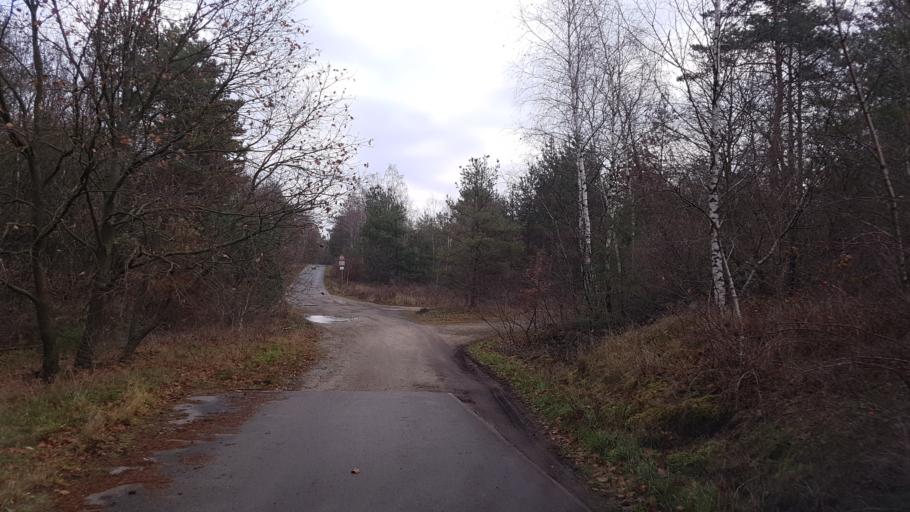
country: DE
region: Brandenburg
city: Sallgast
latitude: 51.5885
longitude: 13.8238
